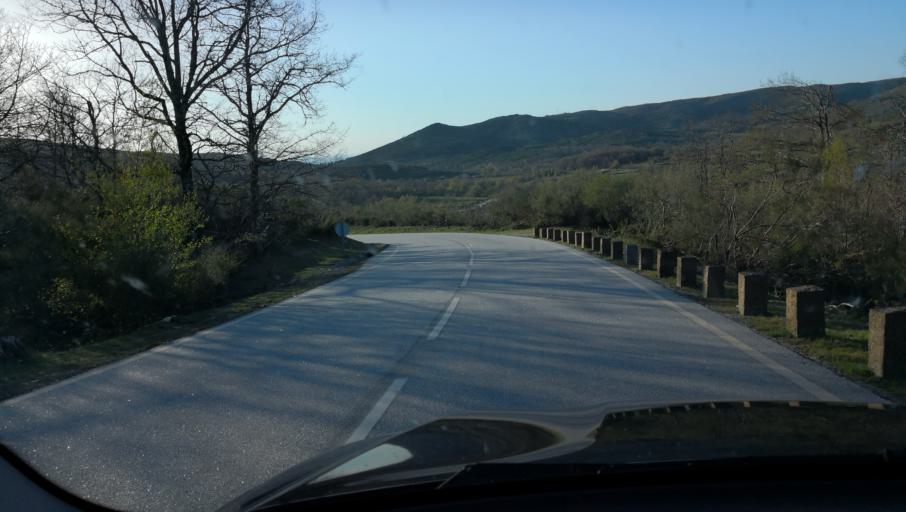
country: PT
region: Vila Real
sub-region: Vila Real
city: Vila Real
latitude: 41.3633
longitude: -7.7972
